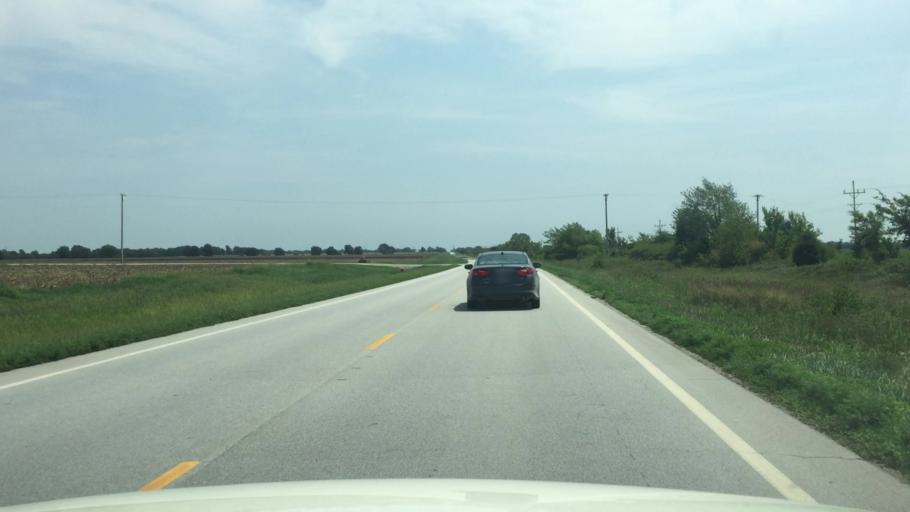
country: US
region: Kansas
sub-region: Cherokee County
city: Columbus
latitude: 37.1794
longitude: -94.9386
